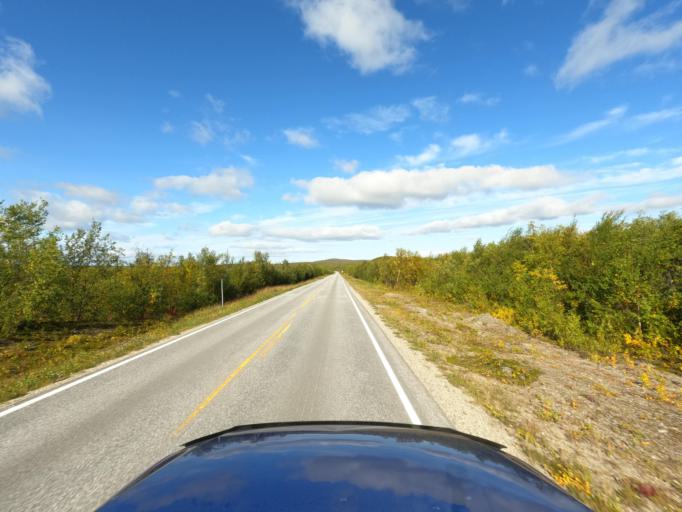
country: NO
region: Finnmark Fylke
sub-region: Karasjok
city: Karasjohka
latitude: 69.5333
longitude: 25.4358
